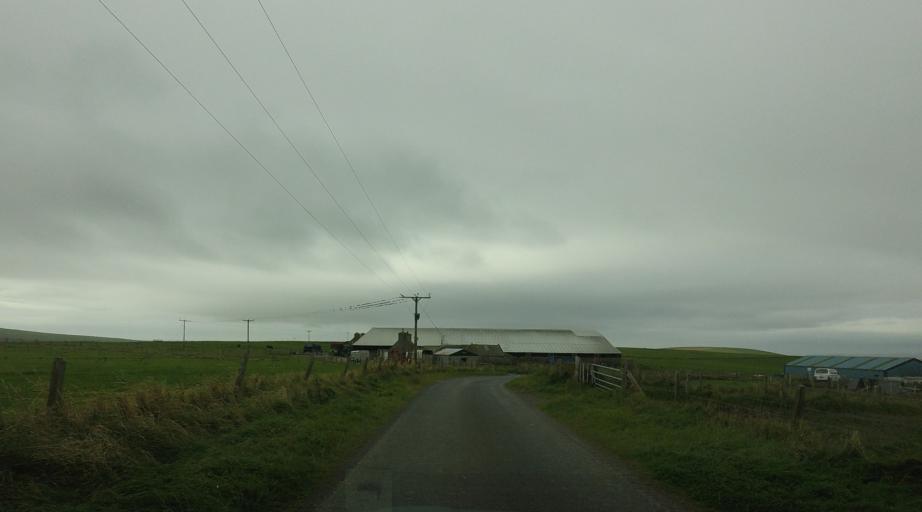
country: GB
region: Scotland
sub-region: Orkney Islands
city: Orkney
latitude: 58.8015
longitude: -2.9439
